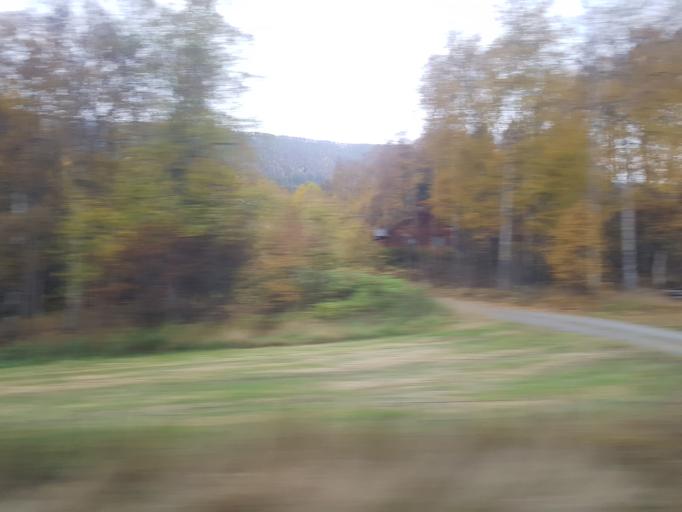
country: NO
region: Oppland
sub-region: Dovre
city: Dovre
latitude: 61.9224
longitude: 9.3385
